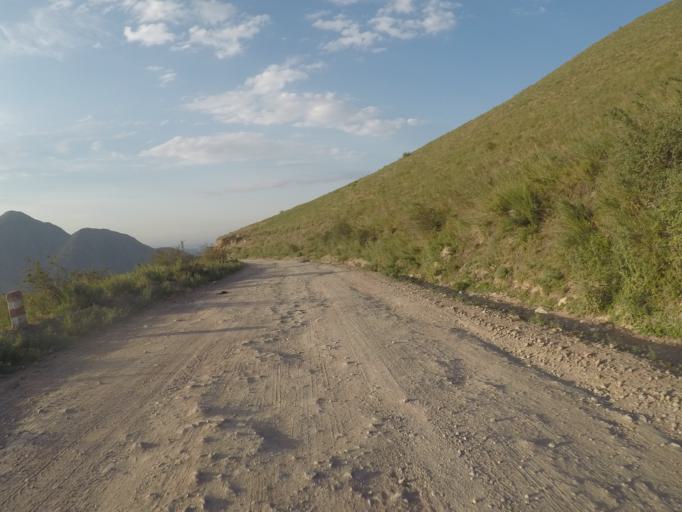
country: KG
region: Chuy
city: Bishkek
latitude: 42.6546
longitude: 74.6629
